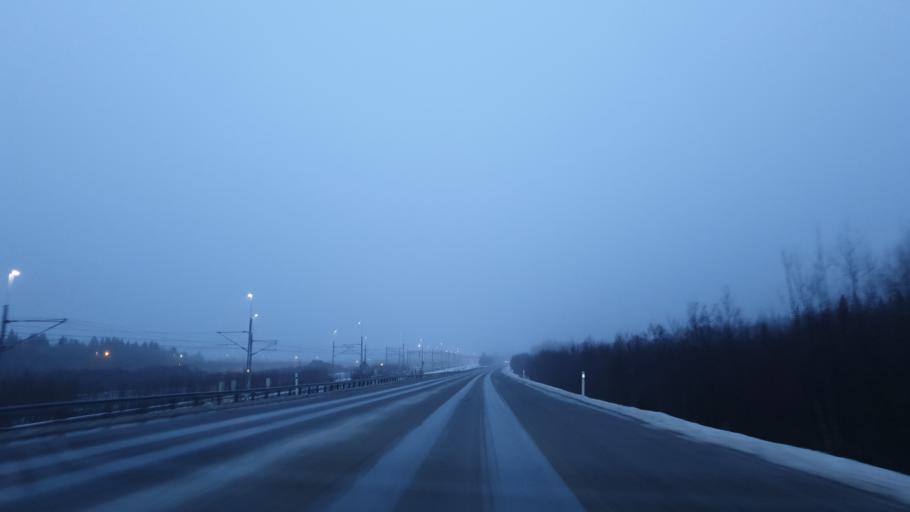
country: SE
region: Vaesterbotten
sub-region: Umea Kommun
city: Umea
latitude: 63.7816
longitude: 20.3222
